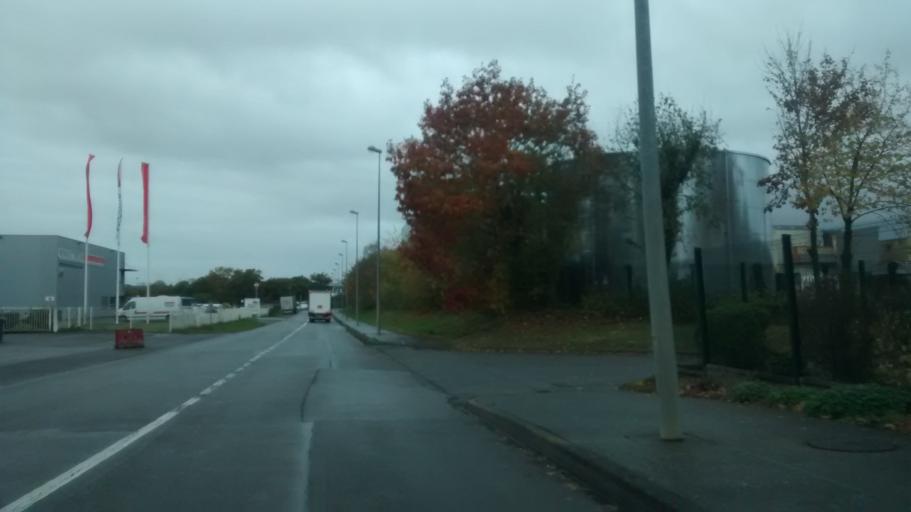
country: FR
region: Brittany
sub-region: Departement d'Ille-et-Vilaine
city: Noyal-sur-Vilaine
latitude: 48.1040
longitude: -1.5073
